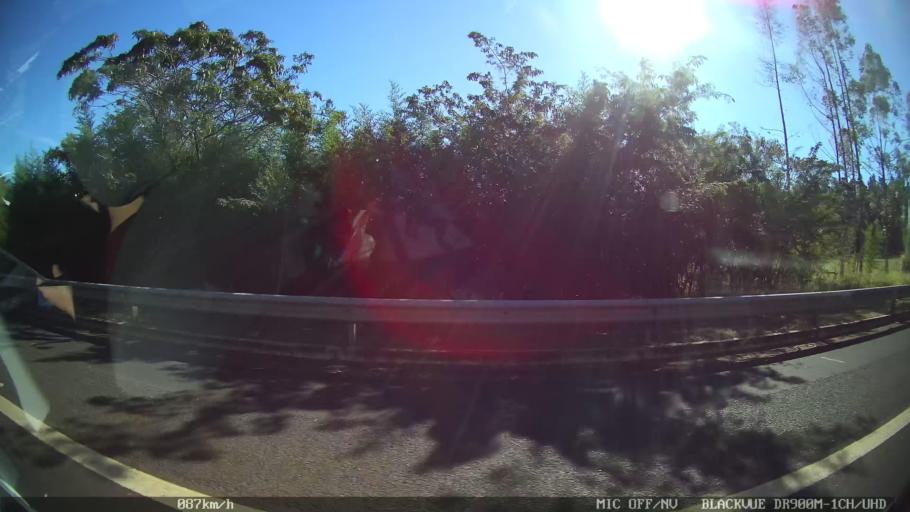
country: BR
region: Sao Paulo
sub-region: Franca
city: Franca
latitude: -20.5766
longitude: -47.3532
